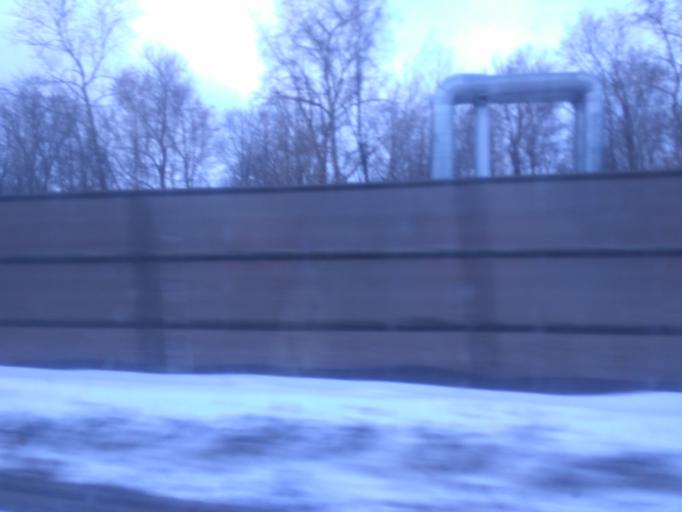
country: RU
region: Moscow
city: Taganskiy
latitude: 55.7315
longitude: 37.6953
